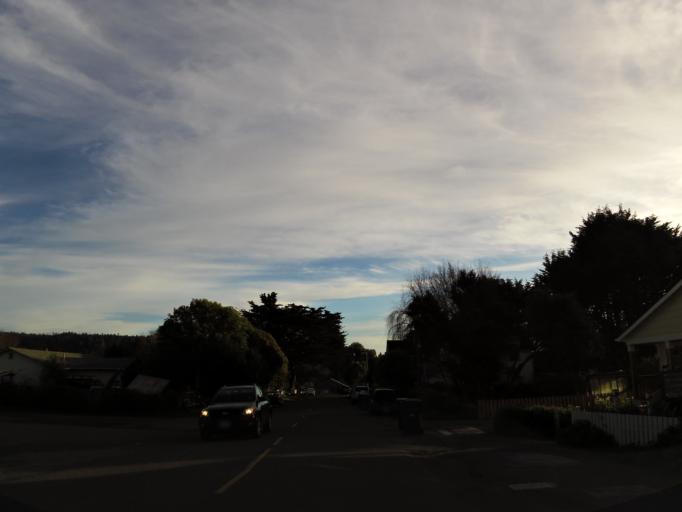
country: US
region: California
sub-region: Mendocino County
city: Fort Bragg
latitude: 39.3074
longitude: -123.7979
